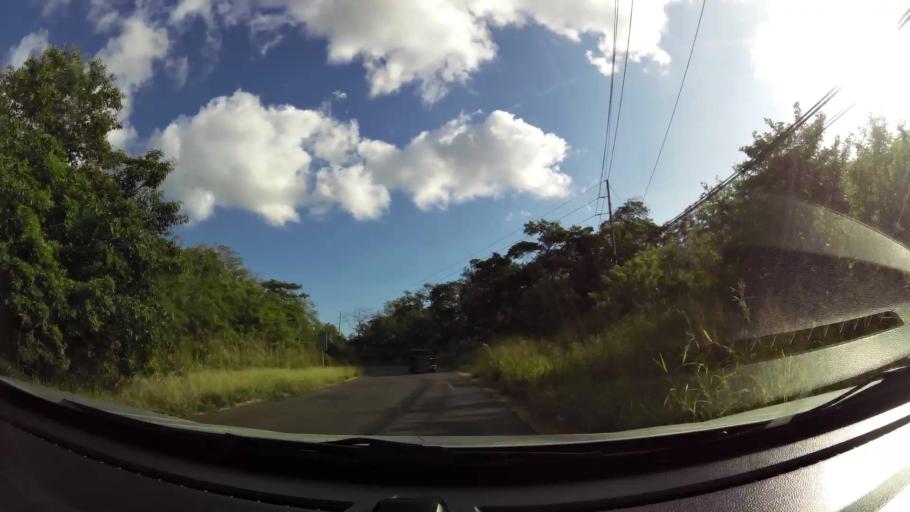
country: CR
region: Guanacaste
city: Sardinal
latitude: 10.5507
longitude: -85.6797
